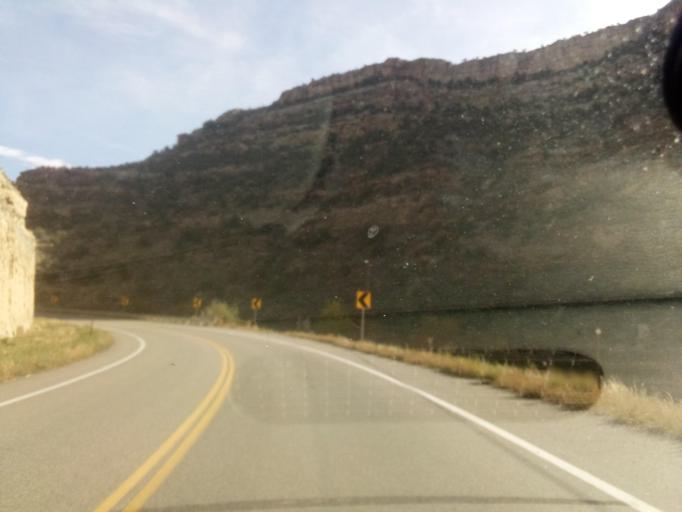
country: US
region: Colorado
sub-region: Mesa County
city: Palisade
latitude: 39.1841
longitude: -108.2662
